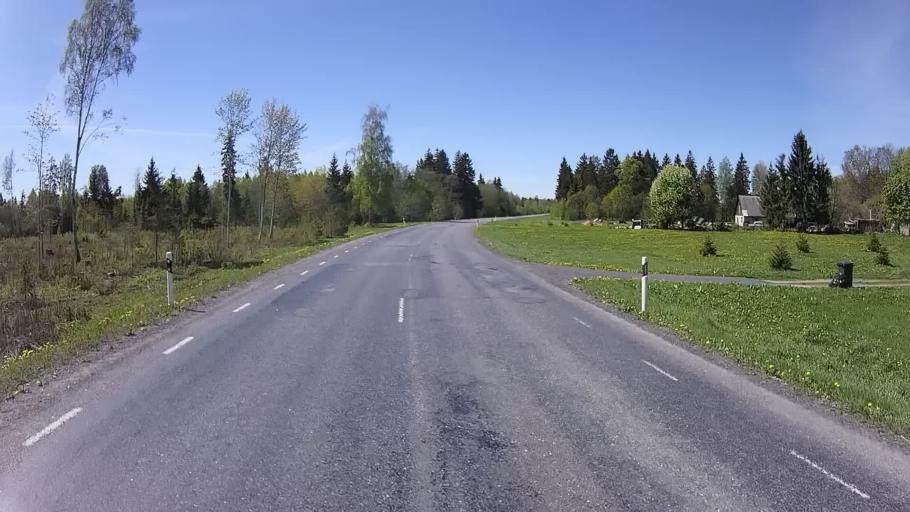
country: EE
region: Raplamaa
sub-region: Kehtna vald
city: Kehtna
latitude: 59.0542
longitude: 24.9674
